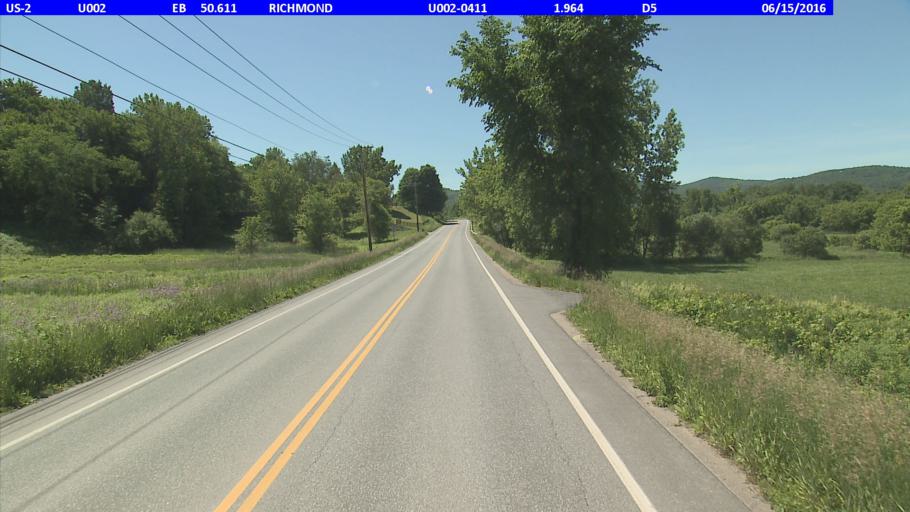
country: US
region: Vermont
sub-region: Chittenden County
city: Williston
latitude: 44.4141
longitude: -72.9992
